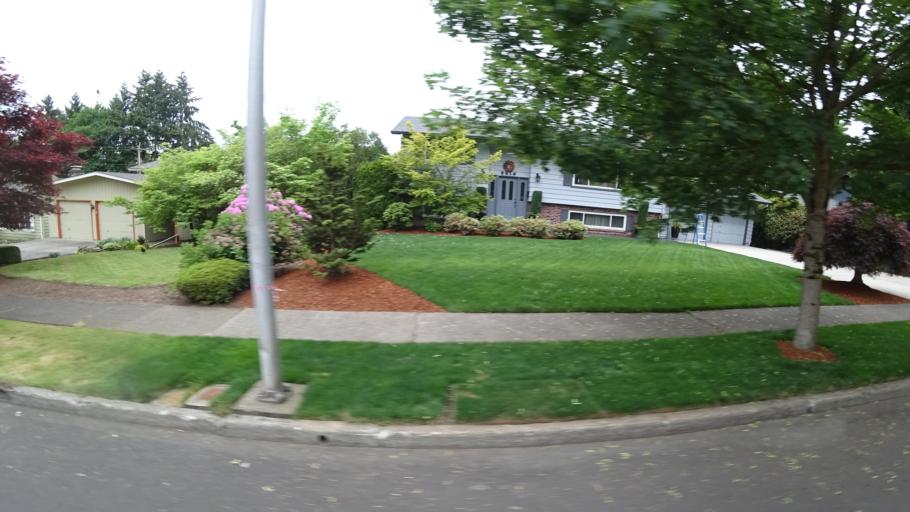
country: US
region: Oregon
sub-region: Washington County
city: Raleigh Hills
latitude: 45.4752
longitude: -122.7749
